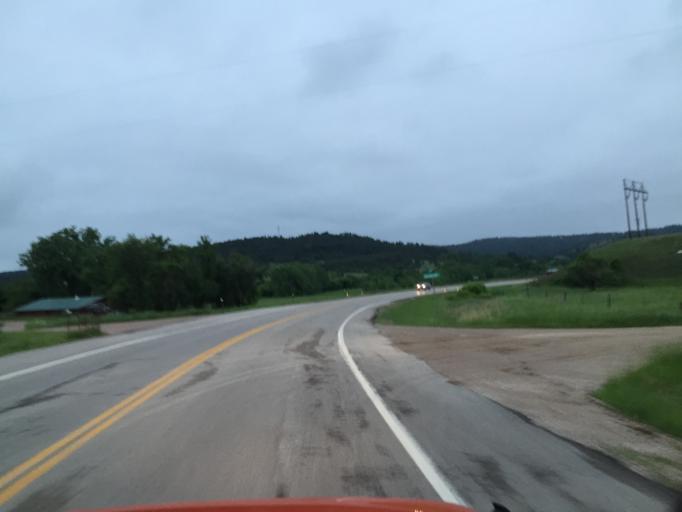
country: US
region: South Dakota
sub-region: Pennington County
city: Colonial Pine Hills
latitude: 43.8310
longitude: -103.2235
